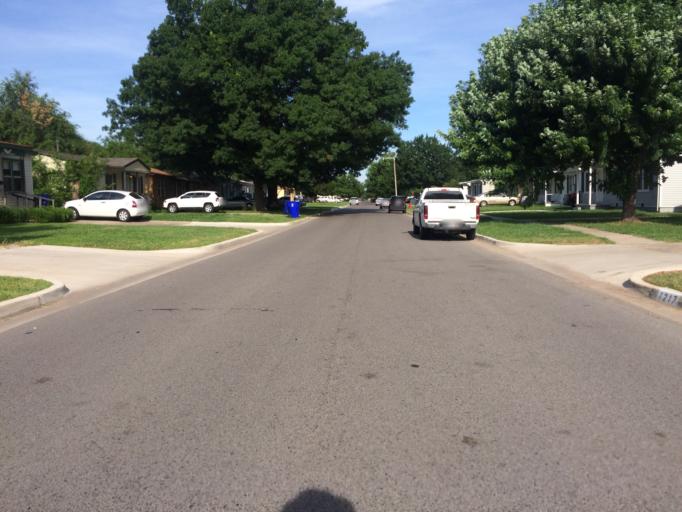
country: US
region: Oklahoma
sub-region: Cleveland County
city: Norman
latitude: 35.2244
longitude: -97.4604
